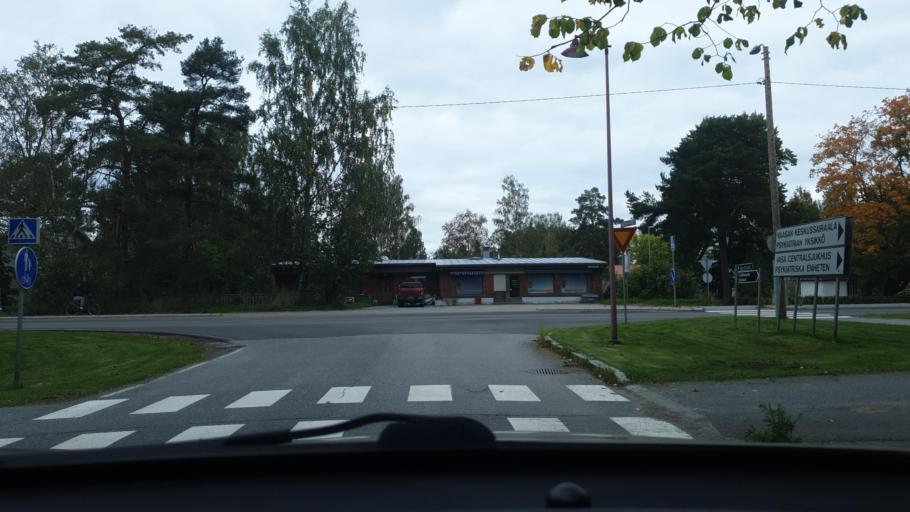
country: FI
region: Ostrobothnia
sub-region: Vaasa
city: Teeriniemi
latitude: 63.0899
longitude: 21.6742
